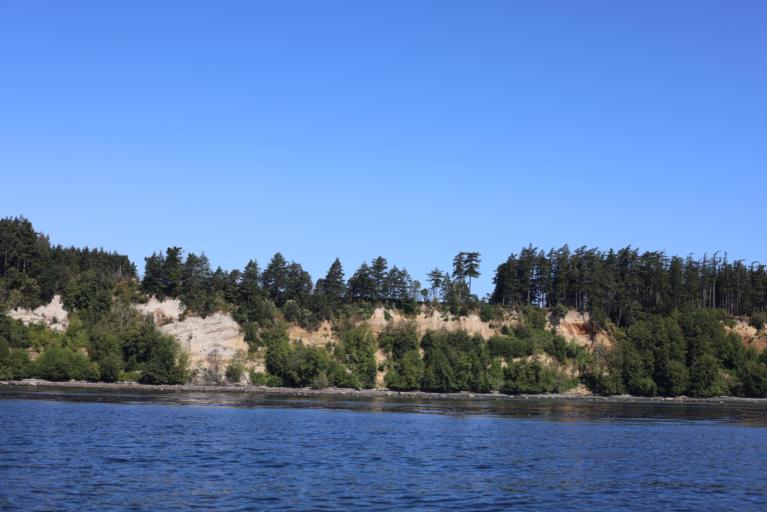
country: CA
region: British Columbia
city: Metchosin
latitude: 48.3755
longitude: -123.5155
